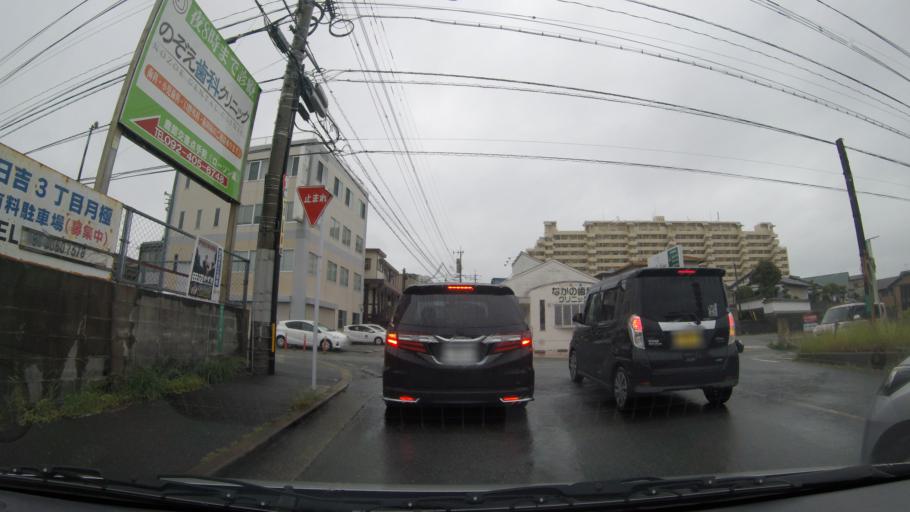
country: JP
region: Fukuoka
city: Koga
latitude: 33.7245
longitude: 130.4584
